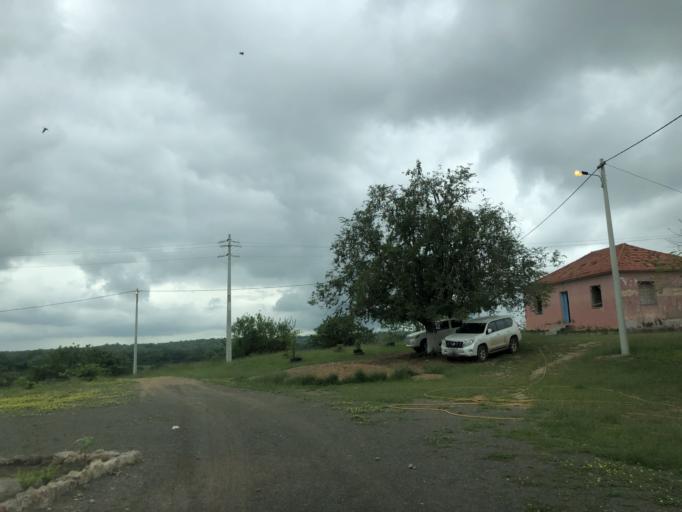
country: AO
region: Cuanza Norte
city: N'dalatando
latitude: -9.6282
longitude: 14.2550
